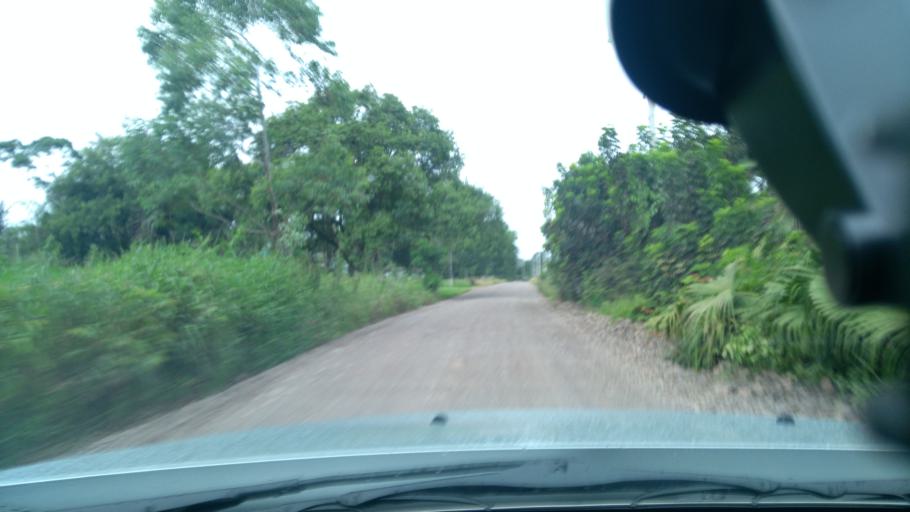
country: BR
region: Rio Grande do Sul
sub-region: Torres
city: Torres
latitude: -29.2074
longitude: -49.9753
